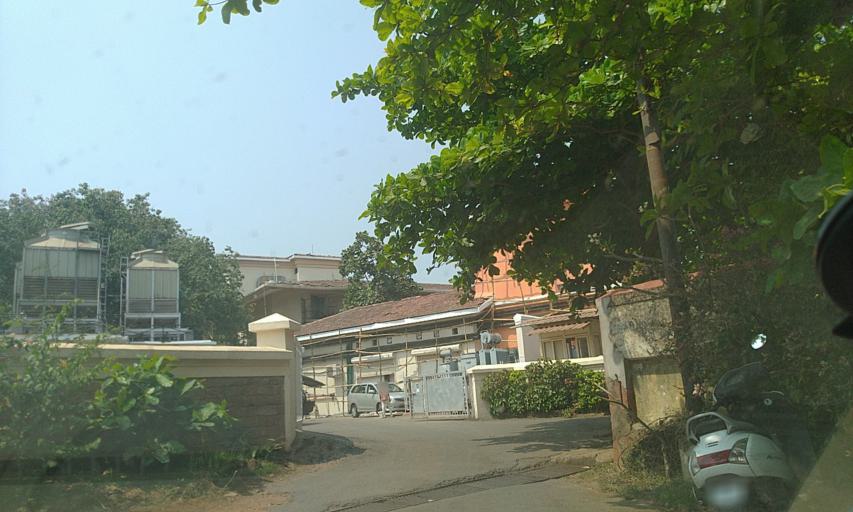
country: IN
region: Goa
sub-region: North Goa
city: Panaji
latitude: 15.4878
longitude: 73.8103
